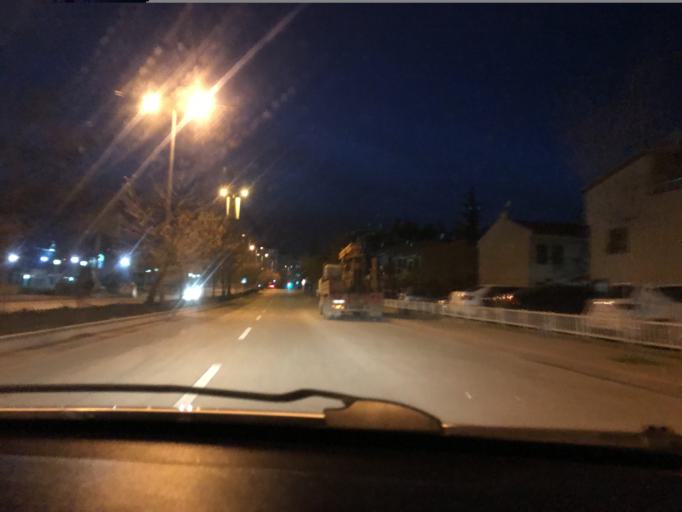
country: TR
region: Ankara
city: Batikent
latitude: 39.9602
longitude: 32.7396
